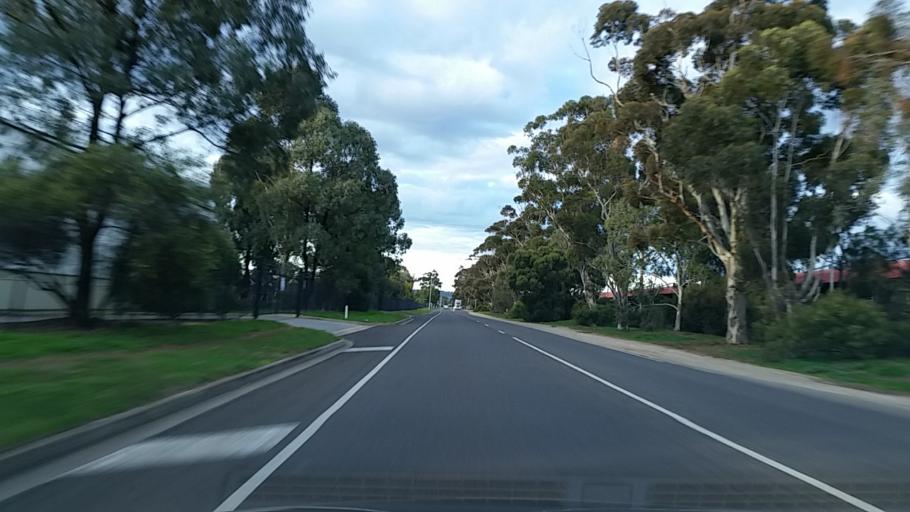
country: AU
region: South Australia
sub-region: Port Adelaide Enfield
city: Enfield
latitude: -34.8296
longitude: 138.6066
